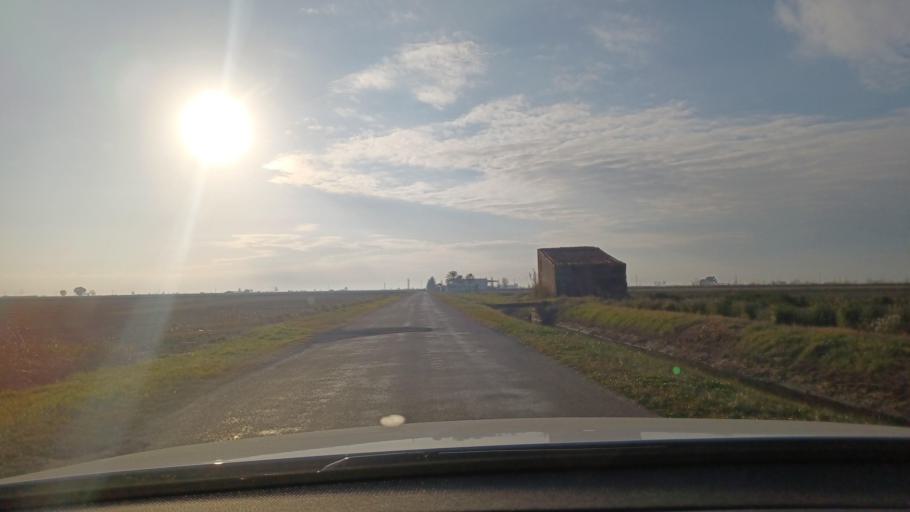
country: ES
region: Catalonia
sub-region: Provincia de Tarragona
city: Deltebre
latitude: 40.6860
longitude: 0.6539
